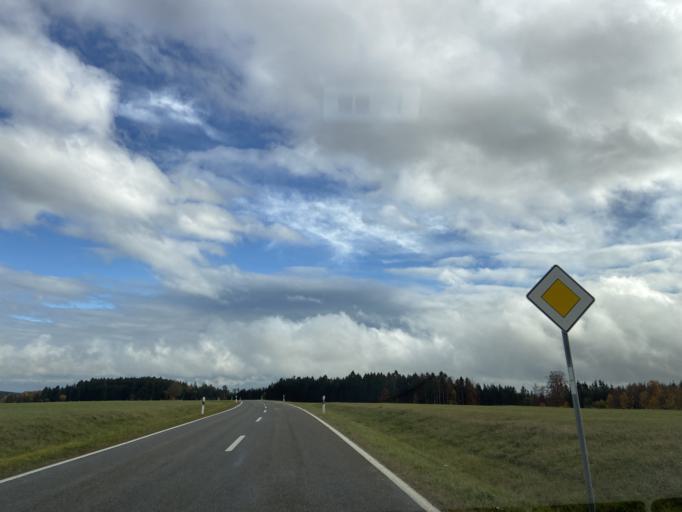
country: DE
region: Baden-Wuerttemberg
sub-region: Tuebingen Region
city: Leibertingen
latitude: 48.0541
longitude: 9.0650
